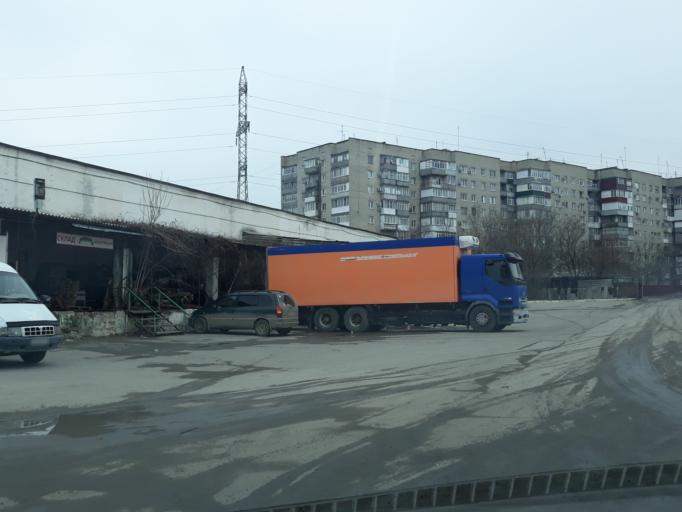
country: RU
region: Rostov
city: Taganrog
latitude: 47.2170
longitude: 38.8760
